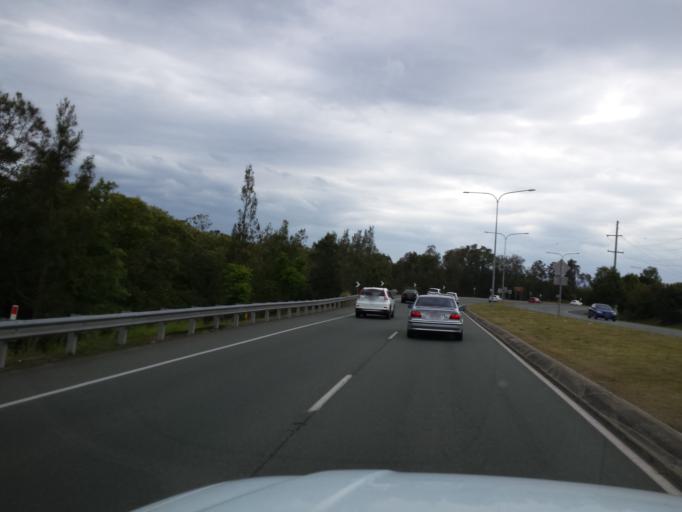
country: AU
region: Queensland
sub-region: Gold Coast
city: Oxenford
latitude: -27.8843
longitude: 153.3225
